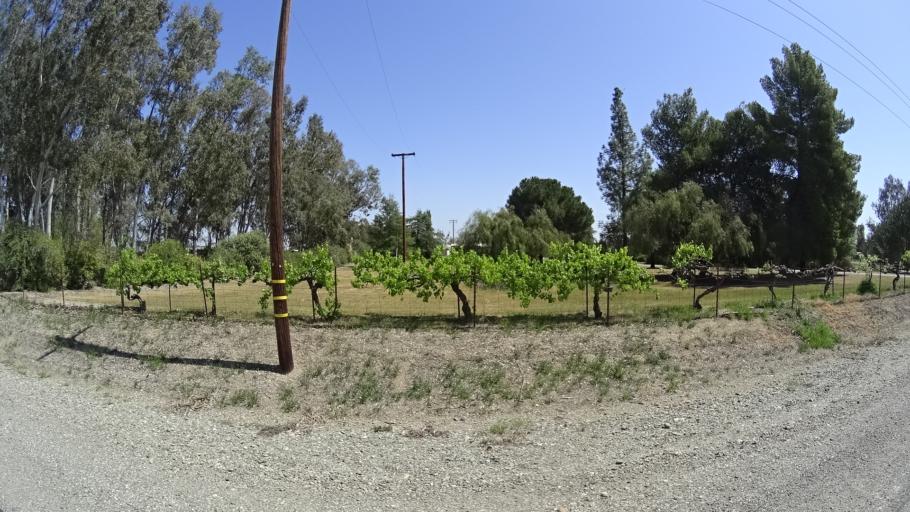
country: US
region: California
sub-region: Glenn County
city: Willows
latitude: 39.6282
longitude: -122.1974
